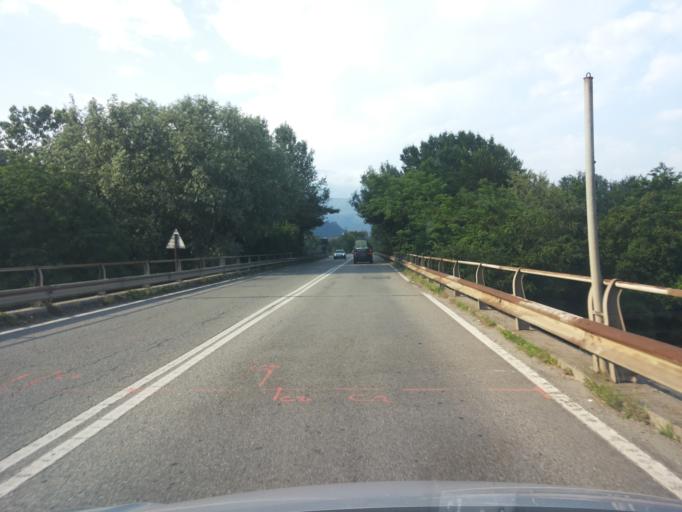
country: IT
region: Piedmont
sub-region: Provincia di Torino
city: Ivrea
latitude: 45.4600
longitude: 7.8857
